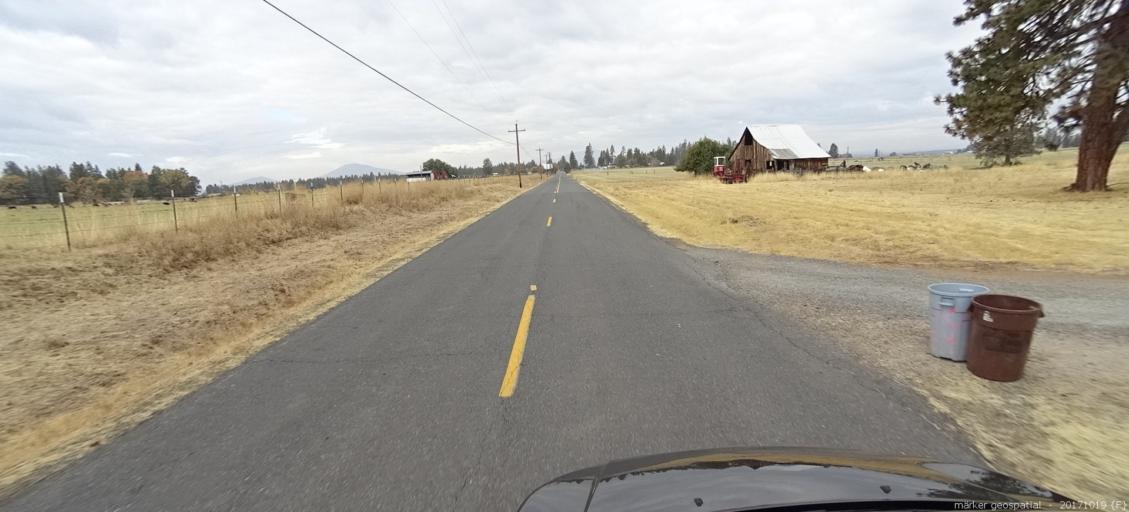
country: US
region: California
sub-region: Shasta County
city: Burney
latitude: 41.0660
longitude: -121.3367
